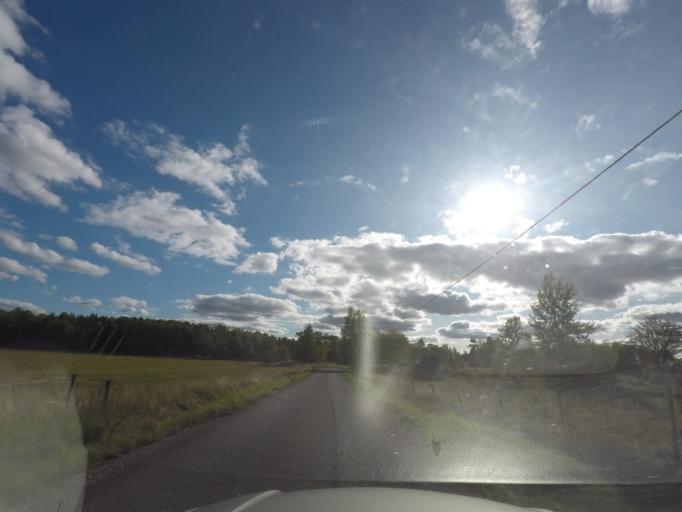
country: SE
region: Vaestmanland
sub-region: Hallstahammars Kommun
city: Kolback
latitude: 59.5003
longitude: 16.1900
